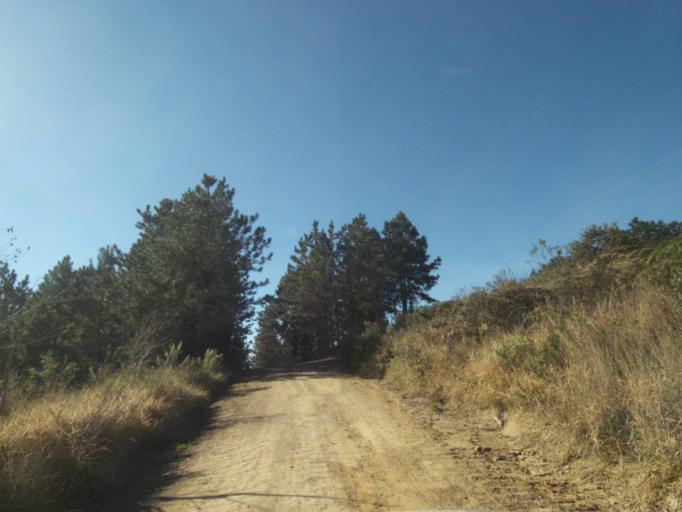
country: BR
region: Parana
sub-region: Tibagi
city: Tibagi
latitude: -24.5700
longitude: -50.4716
